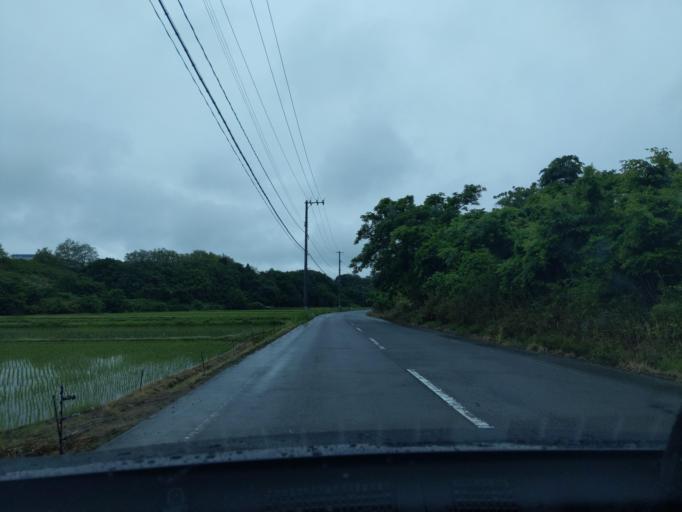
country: JP
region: Fukushima
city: Koriyama
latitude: 37.4434
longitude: 140.2970
